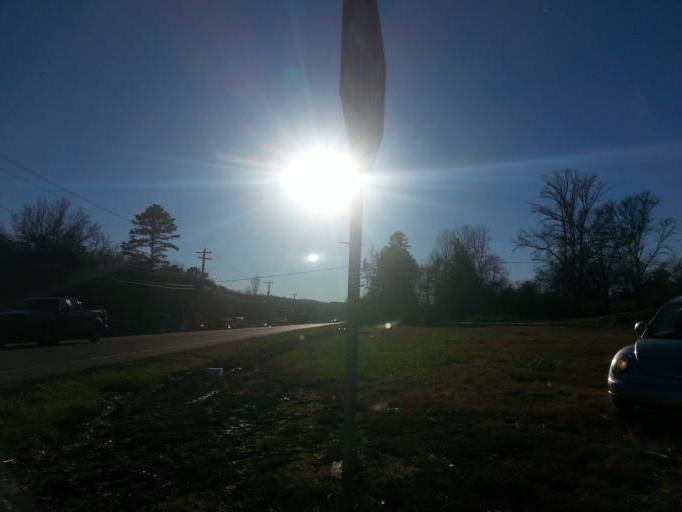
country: US
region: Tennessee
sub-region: Anderson County
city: Oak Ridge
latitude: 36.0431
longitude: -84.2538
